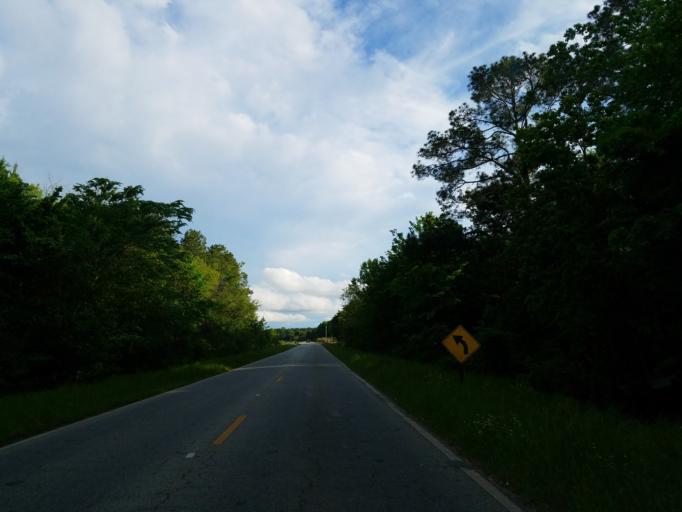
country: US
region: Georgia
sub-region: Crisp County
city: Cordele
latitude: 31.9462
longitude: -83.7876
